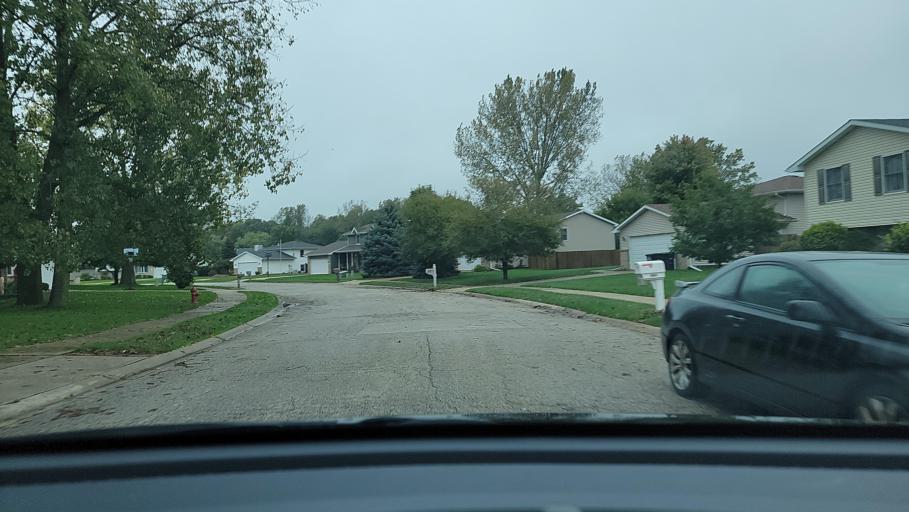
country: US
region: Indiana
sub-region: Porter County
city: Portage
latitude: 41.5451
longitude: -87.1910
